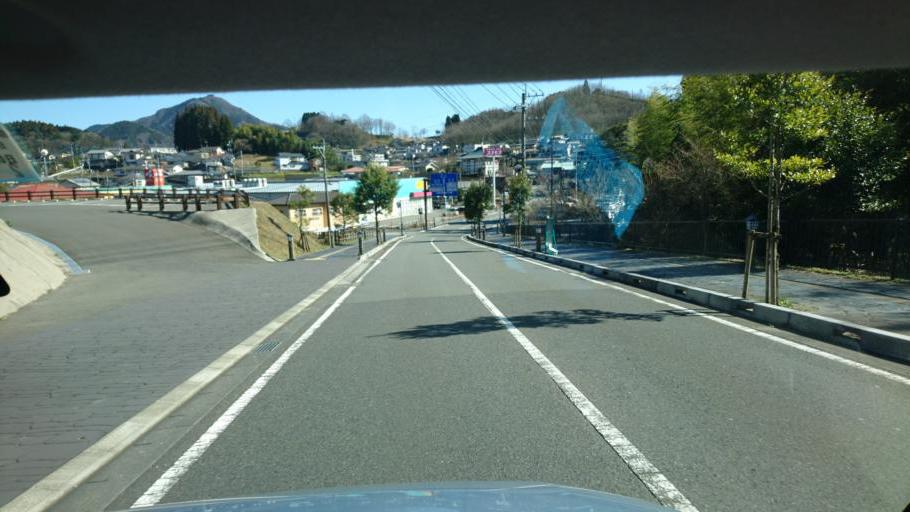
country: JP
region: Oita
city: Takedamachi
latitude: 32.7078
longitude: 131.3023
